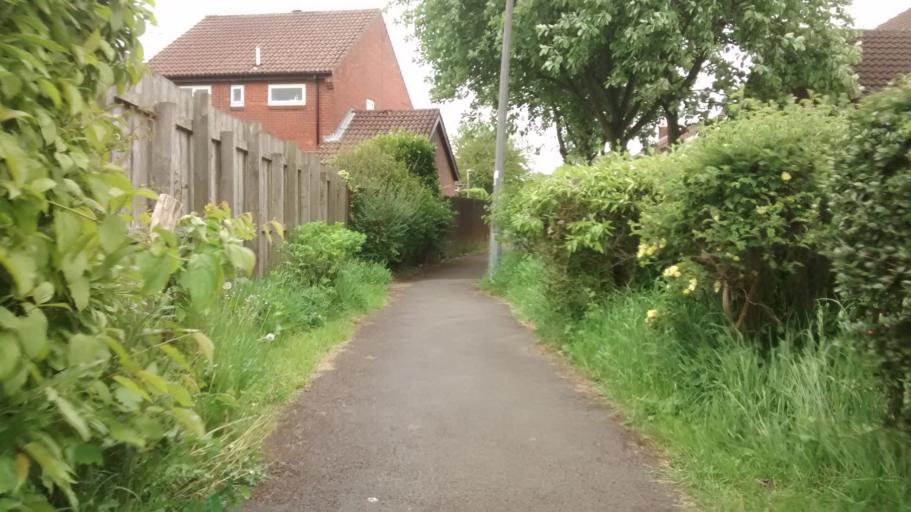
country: GB
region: England
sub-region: County Durham
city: Pittington
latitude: 54.7910
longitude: -1.4919
